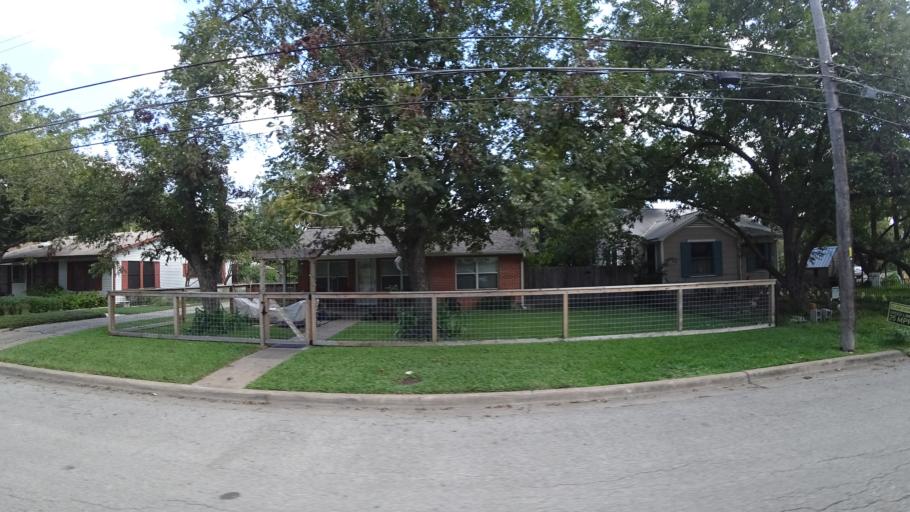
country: US
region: Texas
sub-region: Travis County
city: Austin
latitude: 30.3093
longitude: -97.7184
